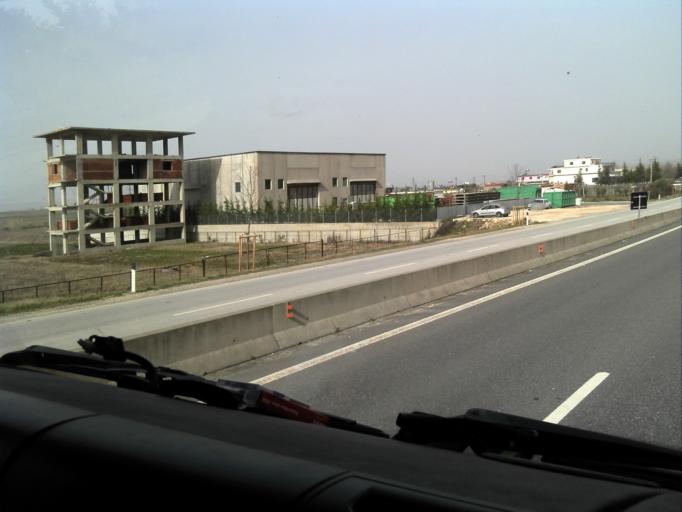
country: AL
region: Tirane
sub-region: Rrethi i Kavajes
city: Rrogozhine
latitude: 41.0388
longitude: 19.6576
